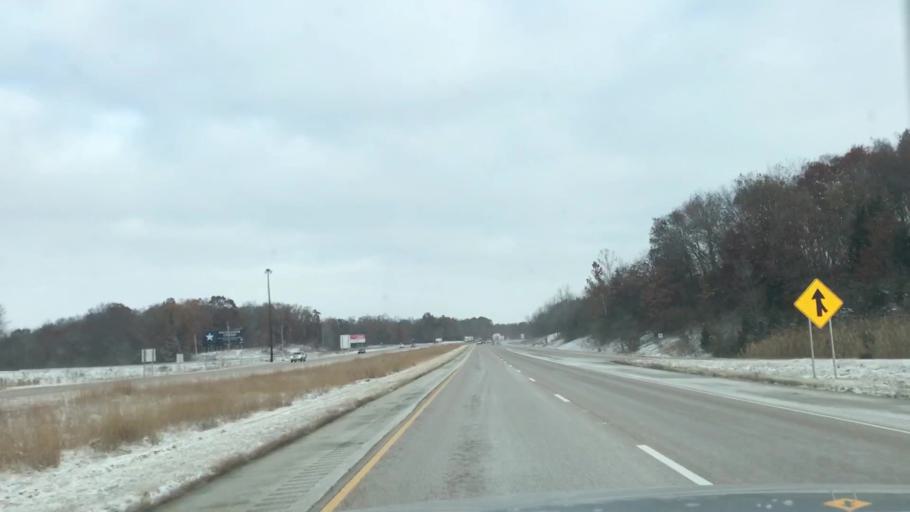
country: US
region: Illinois
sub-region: Macoupin County
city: Mount Olive
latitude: 39.0745
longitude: -89.7555
